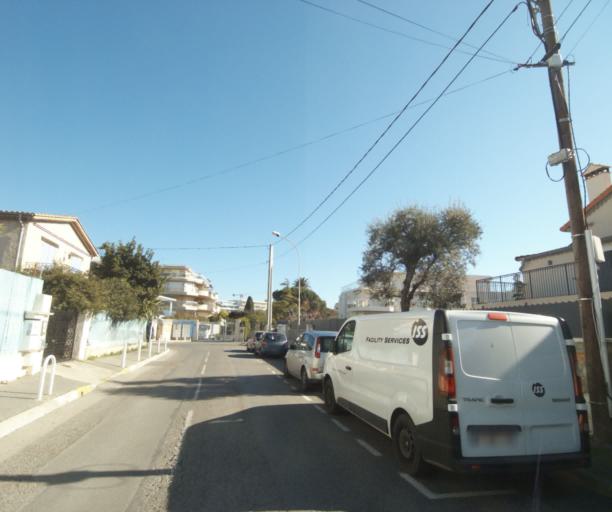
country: FR
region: Provence-Alpes-Cote d'Azur
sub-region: Departement des Alpes-Maritimes
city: Antibes
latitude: 43.5724
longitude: 7.0975
